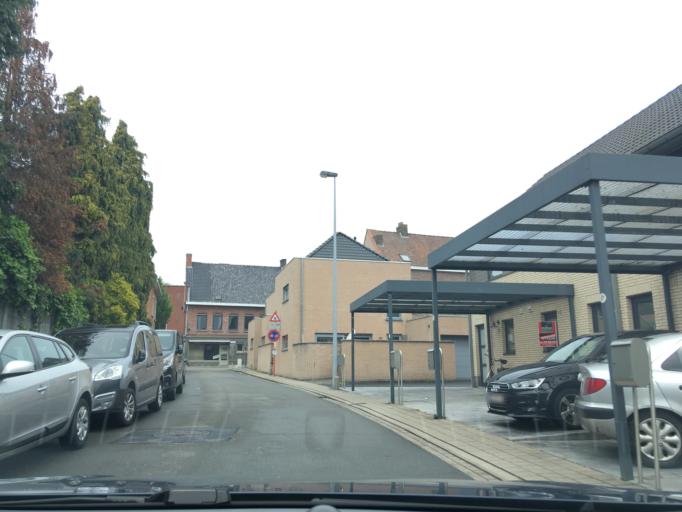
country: BE
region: Flanders
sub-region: Provincie West-Vlaanderen
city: Roeselare
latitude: 50.9318
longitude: 3.1527
